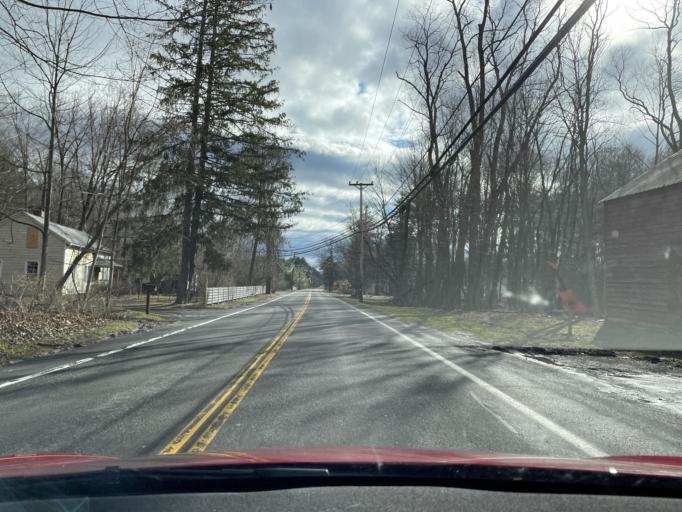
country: US
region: New York
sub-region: Ulster County
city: Woodstock
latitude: 42.0404
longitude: -74.1515
